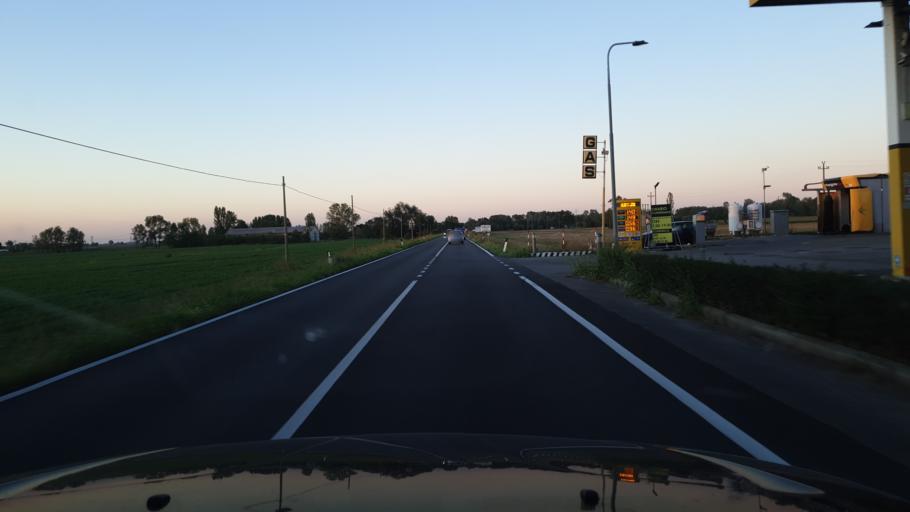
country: IT
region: Emilia-Romagna
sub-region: Provincia di Bologna
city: Granarolo dell'Emilia e Viadagola
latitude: 44.5892
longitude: 11.4311
